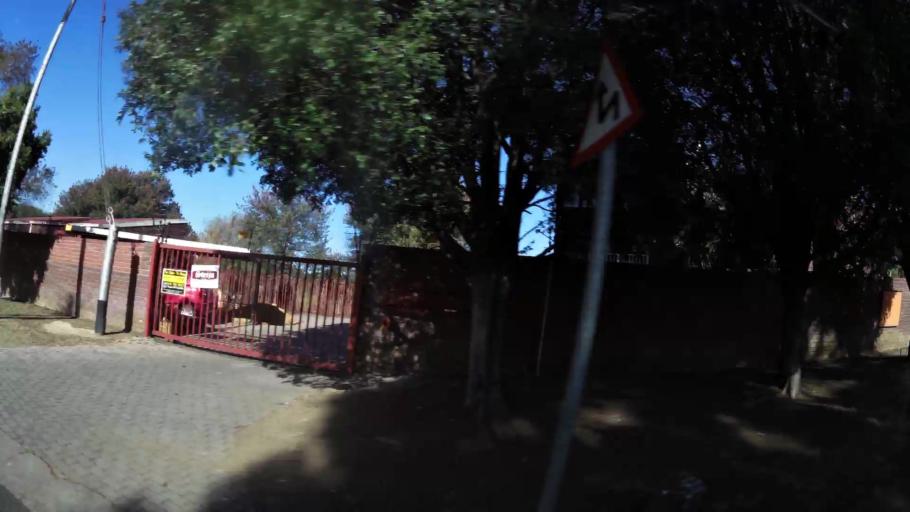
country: ZA
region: Gauteng
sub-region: City of Tshwane Metropolitan Municipality
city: Pretoria
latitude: -25.7138
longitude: 28.2637
